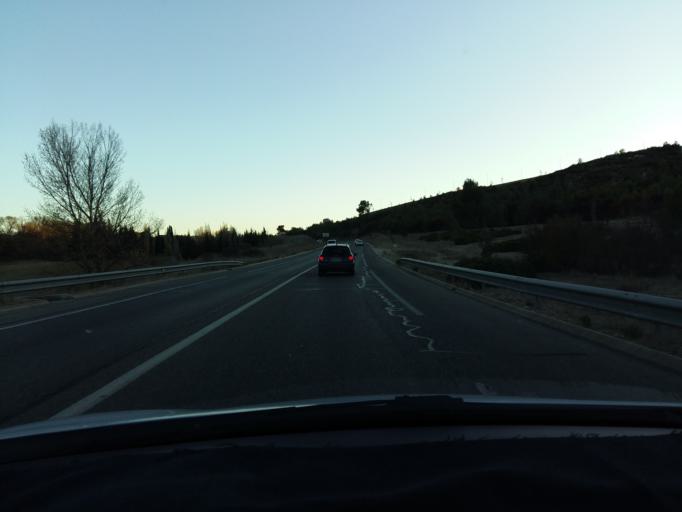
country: FR
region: Provence-Alpes-Cote d'Azur
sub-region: Departement des Bouches-du-Rhone
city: Cabries
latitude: 43.4839
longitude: 5.3537
